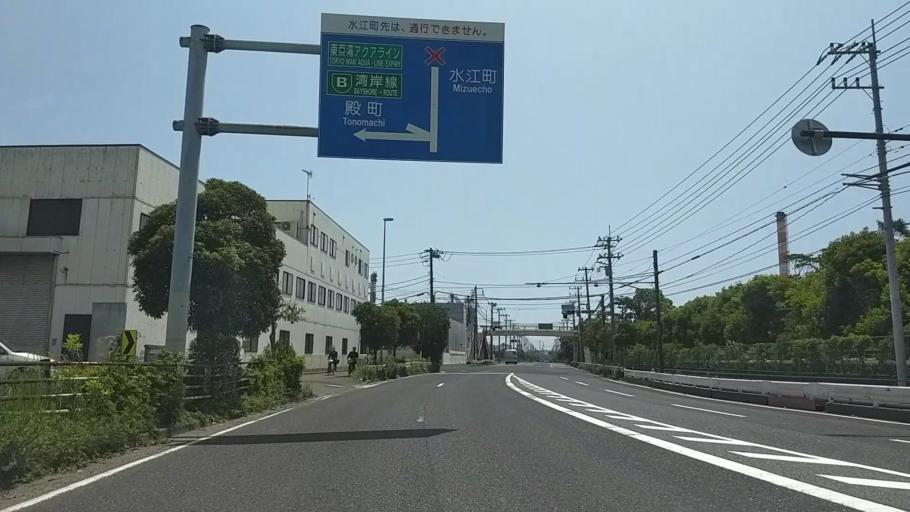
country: JP
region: Kanagawa
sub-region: Kawasaki-shi
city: Kawasaki
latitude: 35.5173
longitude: 139.7361
